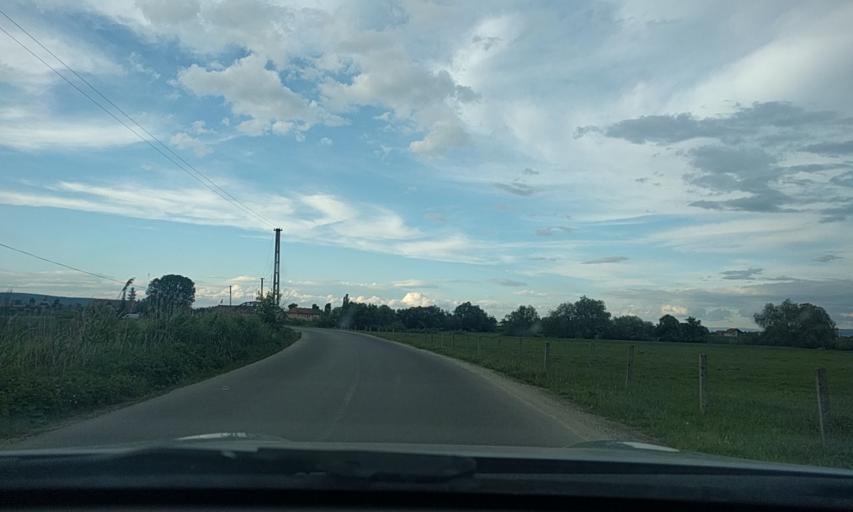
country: RO
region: Brasov
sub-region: Comuna Harman
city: Harman
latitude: 45.7522
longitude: 25.7121
